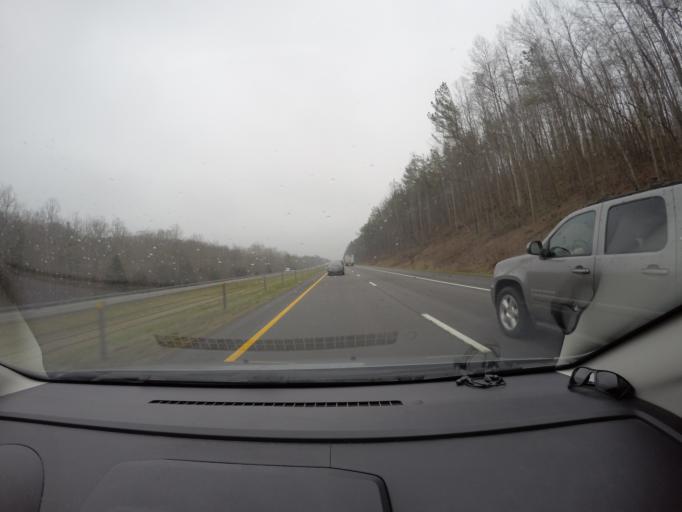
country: US
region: Tennessee
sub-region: Coffee County
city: New Union
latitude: 35.5517
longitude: -86.1938
